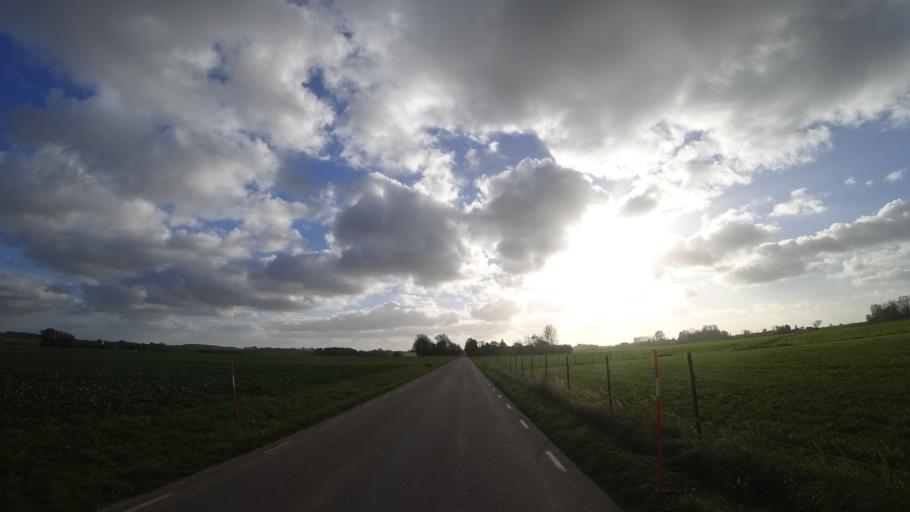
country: SE
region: Skane
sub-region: Staffanstorps Kommun
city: Staffanstorp
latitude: 55.6227
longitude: 13.2184
